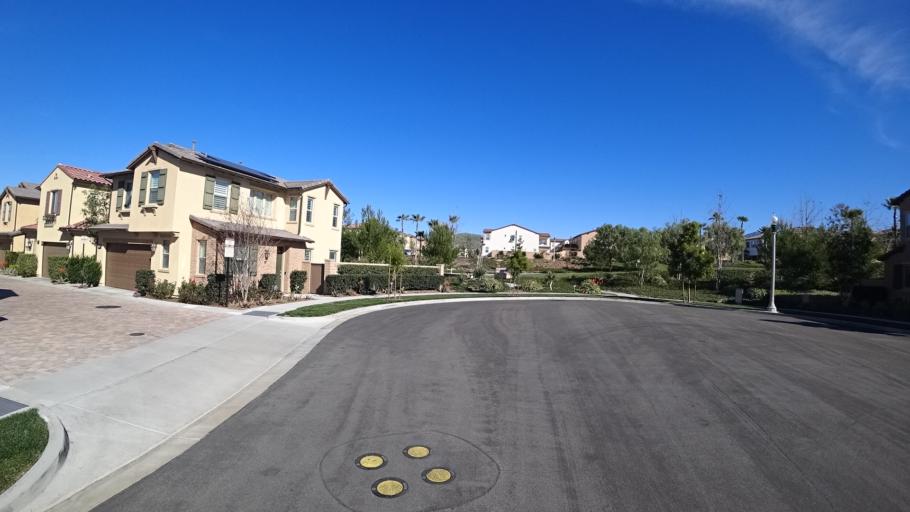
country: US
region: California
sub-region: Orange County
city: Foothill Ranch
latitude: 33.6732
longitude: -117.6812
